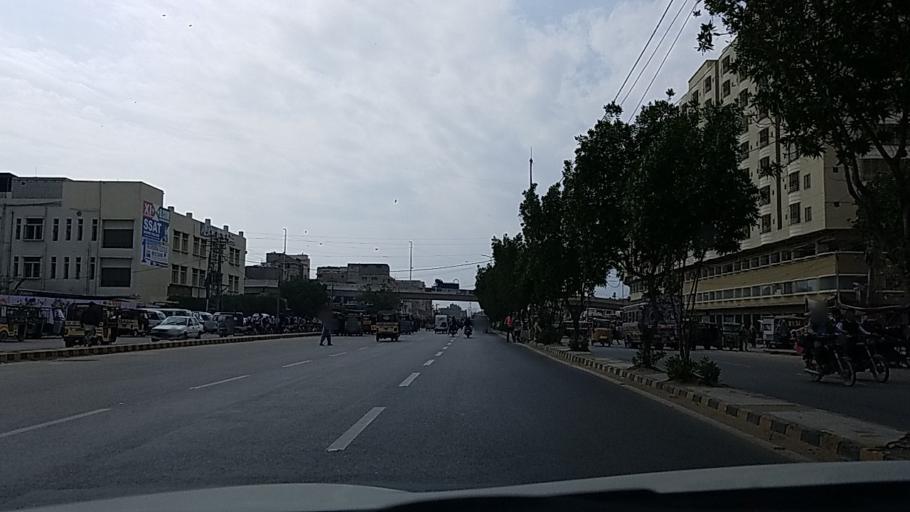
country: PK
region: Sindh
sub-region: Karachi District
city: Karachi
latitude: 24.8174
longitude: 67.1096
